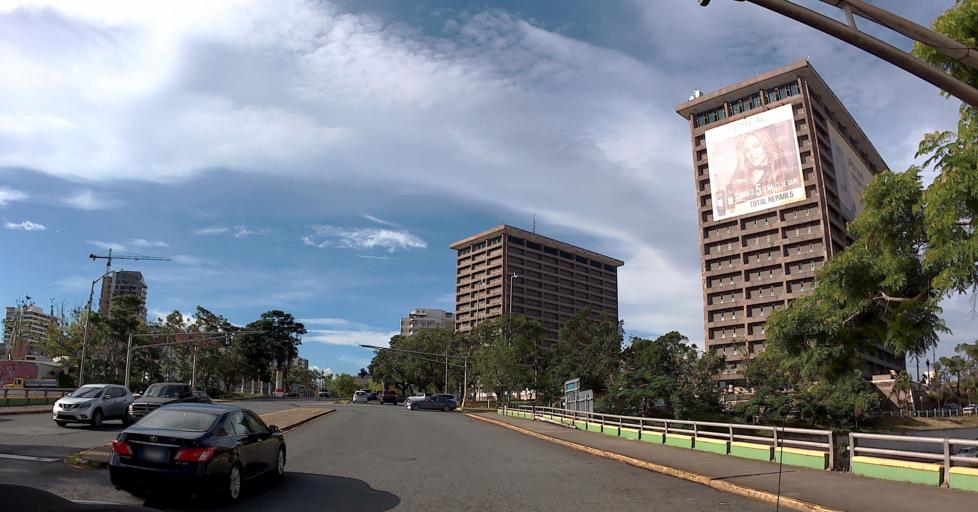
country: PR
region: San Juan
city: San Juan
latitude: 18.4501
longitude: -66.0659
